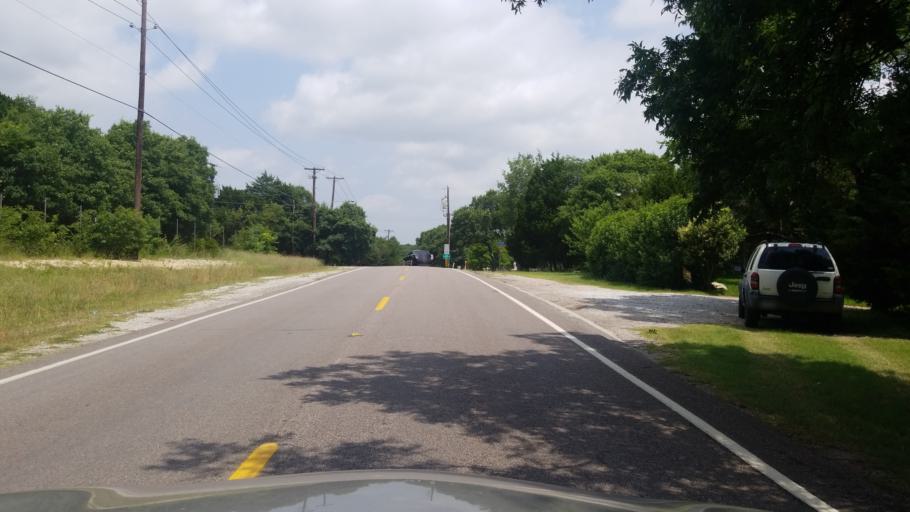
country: US
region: Texas
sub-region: Dallas County
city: Duncanville
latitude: 32.6758
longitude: -96.9257
